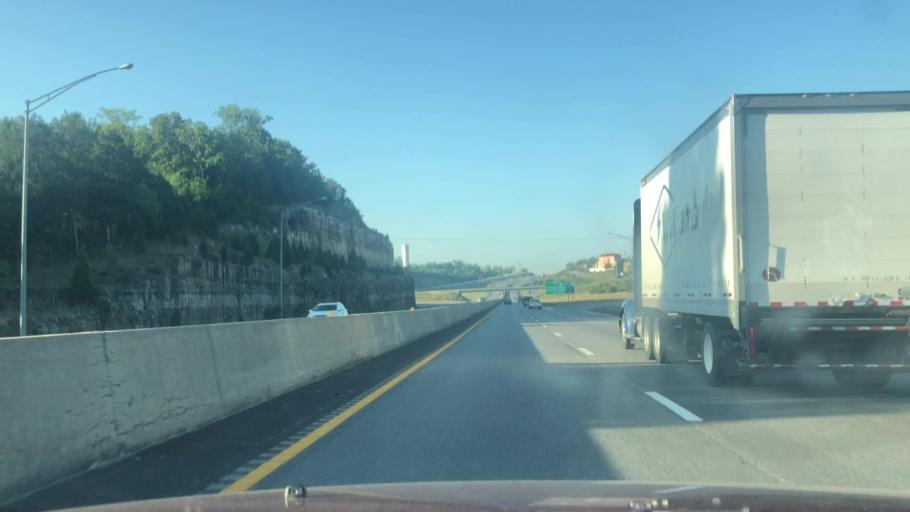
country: US
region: Missouri
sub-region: Taney County
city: Branson
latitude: 36.6741
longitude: -93.2213
